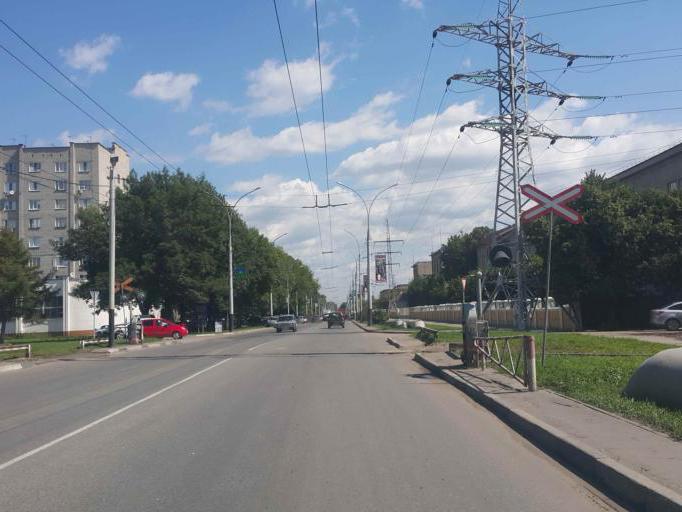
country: RU
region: Tambov
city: Tambov
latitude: 52.7487
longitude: 41.4600
